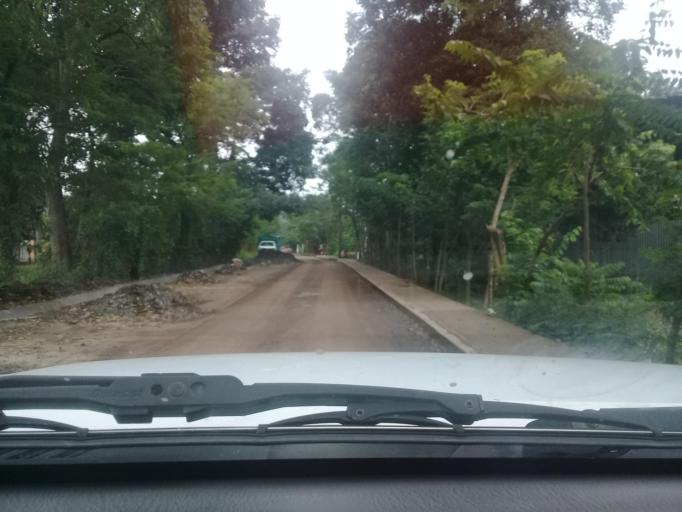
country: MX
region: Veracruz
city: Comoapan
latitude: 18.4111
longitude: -95.1790
